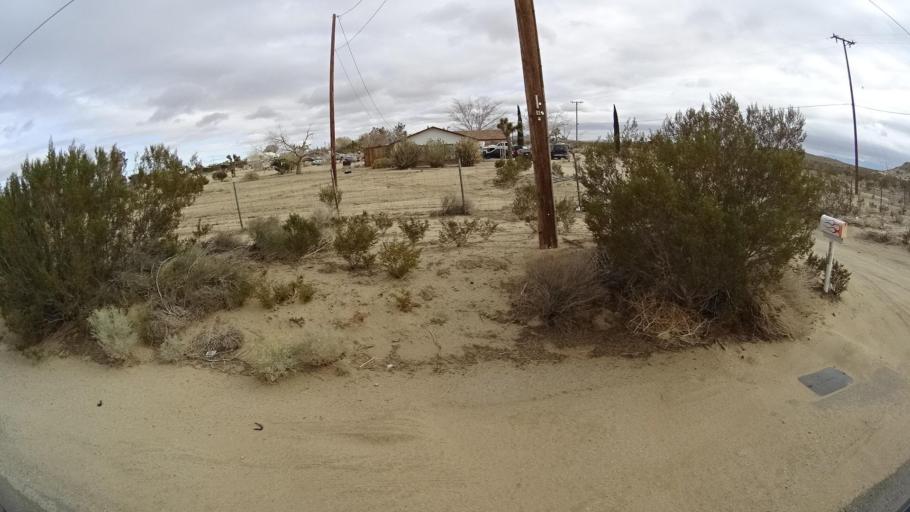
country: US
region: California
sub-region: Kern County
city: Rosamond
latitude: 34.9329
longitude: -118.2124
